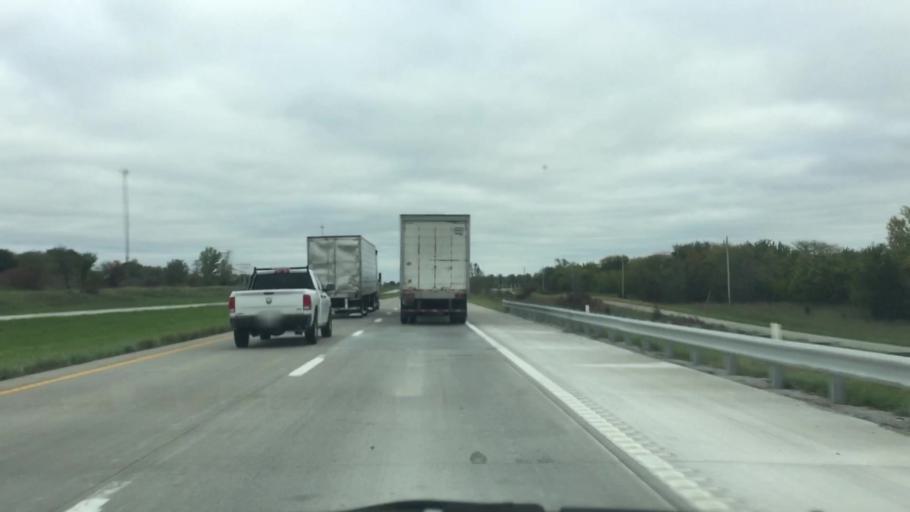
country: US
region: Missouri
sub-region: Clinton County
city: Lathrop
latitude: 39.5972
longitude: -94.2543
